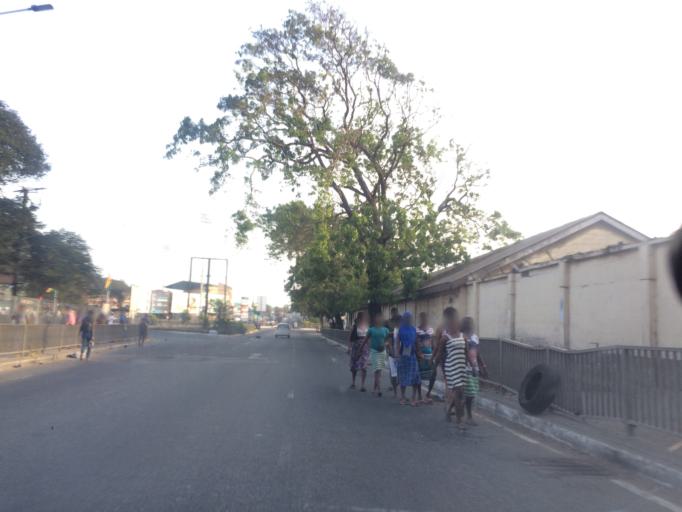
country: GH
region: Greater Accra
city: Accra
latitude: 5.5501
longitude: -0.2040
